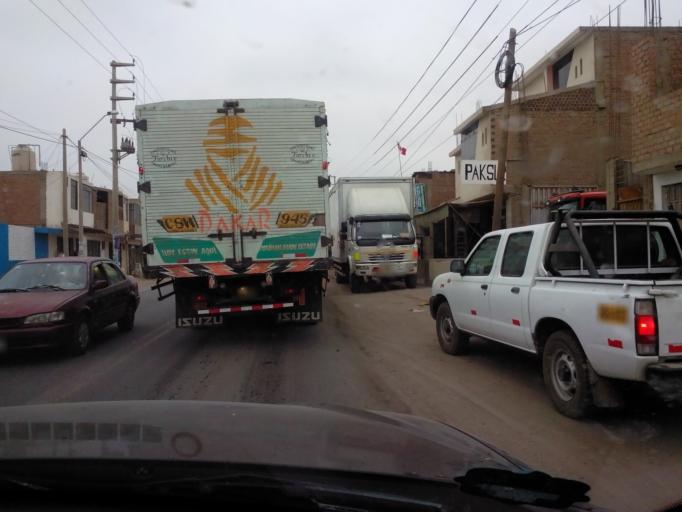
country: PE
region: Ica
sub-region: Provincia de Chincha
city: Chincha Alta
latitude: -13.4344
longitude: -76.1345
